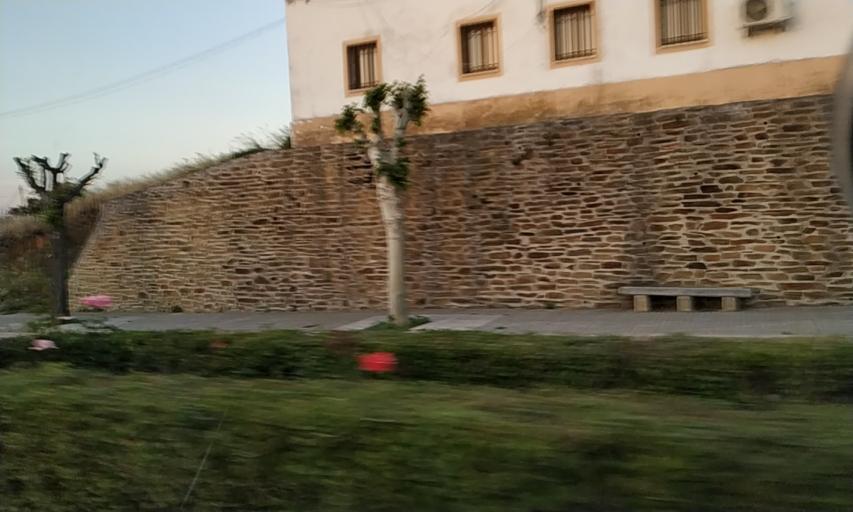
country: ES
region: Extremadura
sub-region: Provincia de Caceres
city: Alcantara
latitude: 39.7103
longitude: -6.8862
